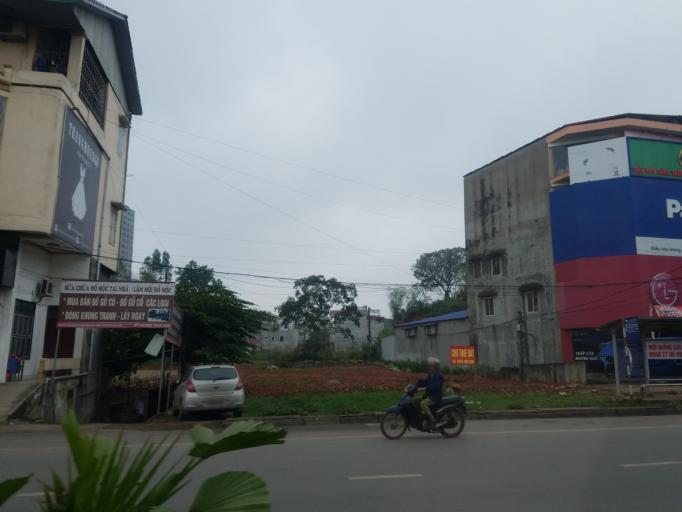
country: VN
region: Thai Nguyen
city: Thanh Pho Thai Nguyen
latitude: 21.5913
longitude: 105.8446
